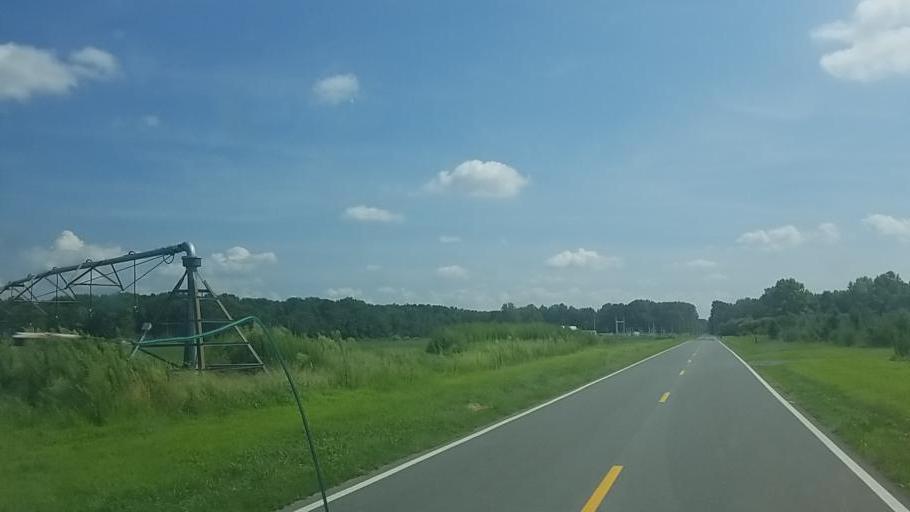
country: US
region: Maryland
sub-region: Wicomico County
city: Hebron
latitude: 38.4289
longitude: -75.6978
